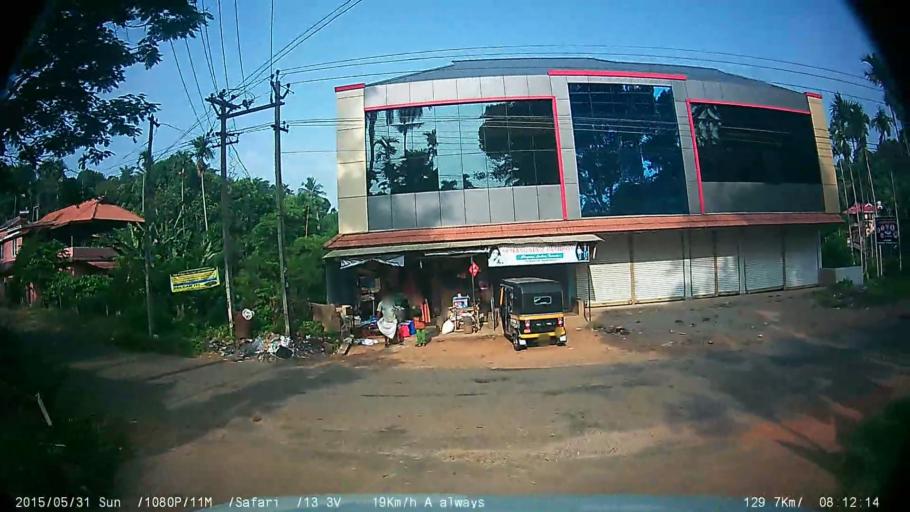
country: IN
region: Kerala
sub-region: Wayanad
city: Kalpetta
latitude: 11.6367
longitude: 76.0143
